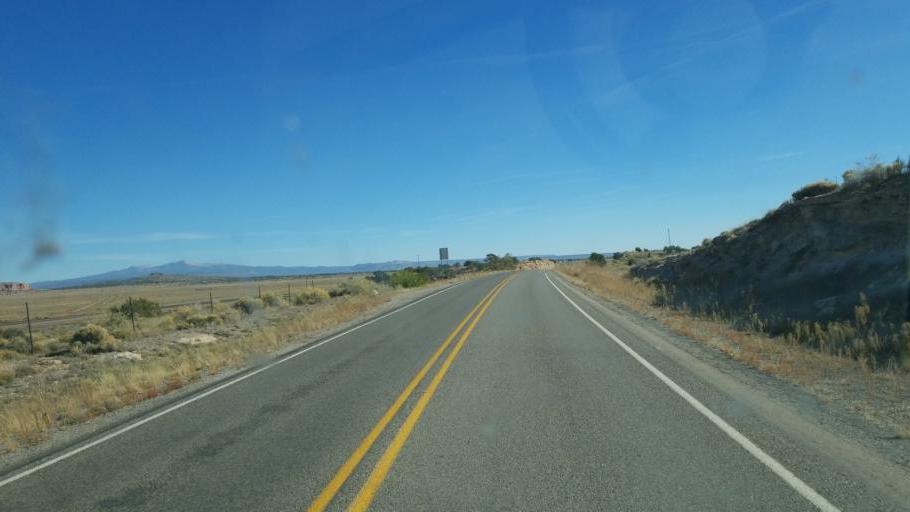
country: US
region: New Mexico
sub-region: McKinley County
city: Thoreau
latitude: 35.3515
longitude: -108.0146
